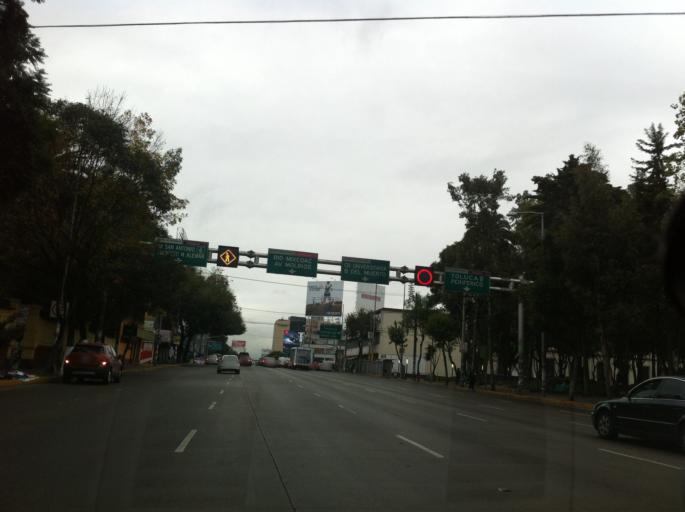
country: MX
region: Mexico City
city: Polanco
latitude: 19.4014
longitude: -99.1847
